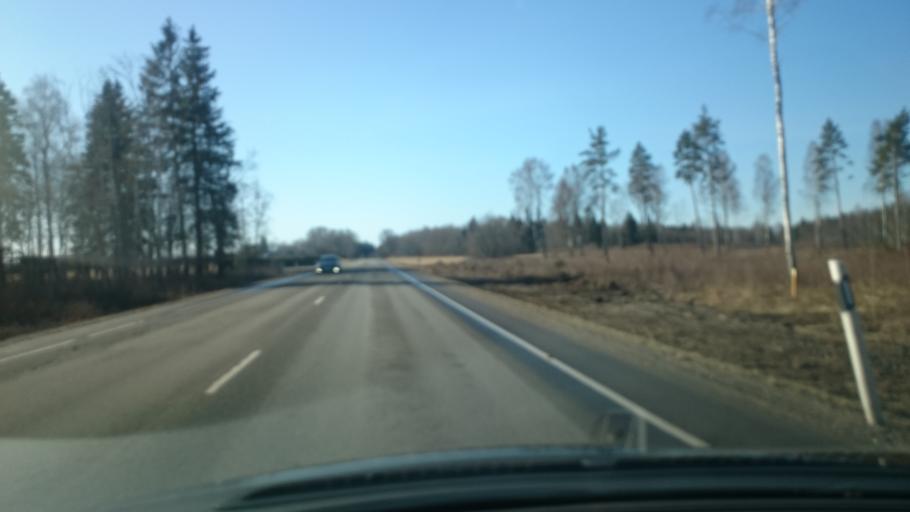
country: EE
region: Harju
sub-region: Saku vald
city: Saku
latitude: 59.2618
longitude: 24.7409
